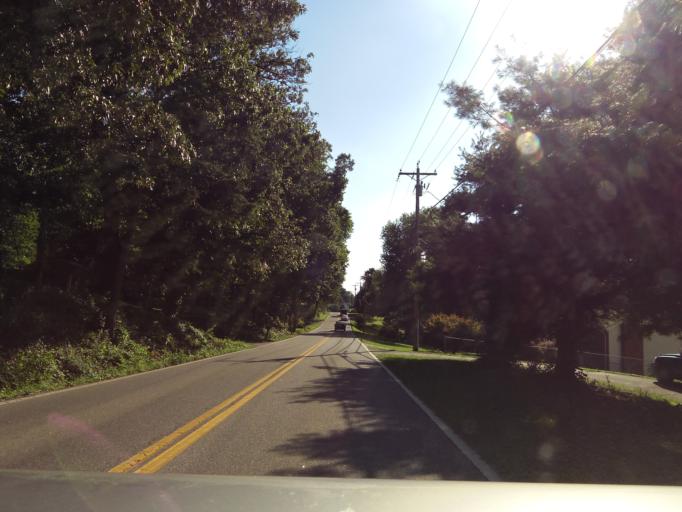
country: US
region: Tennessee
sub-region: Blount County
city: Louisville
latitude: 35.7821
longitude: -84.0216
